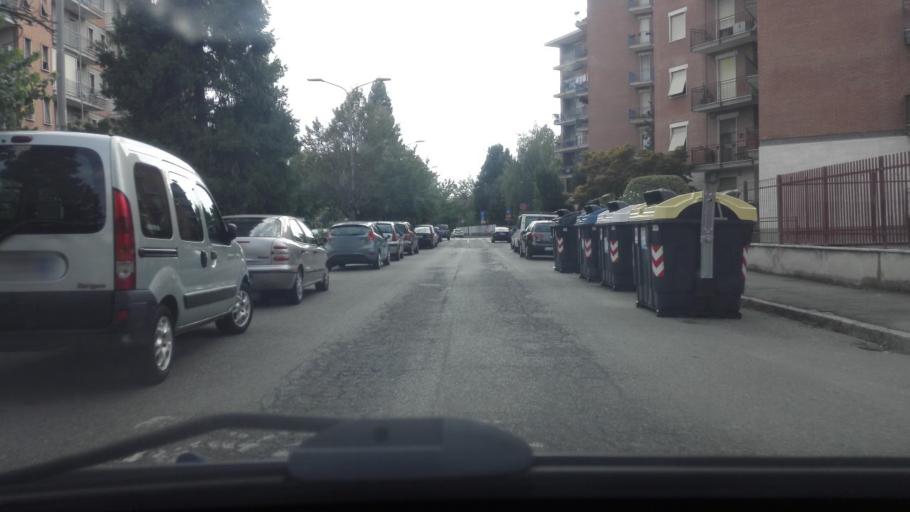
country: IT
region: Piedmont
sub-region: Provincia di Alessandria
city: Alessandria
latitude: 44.8952
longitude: 8.6019
